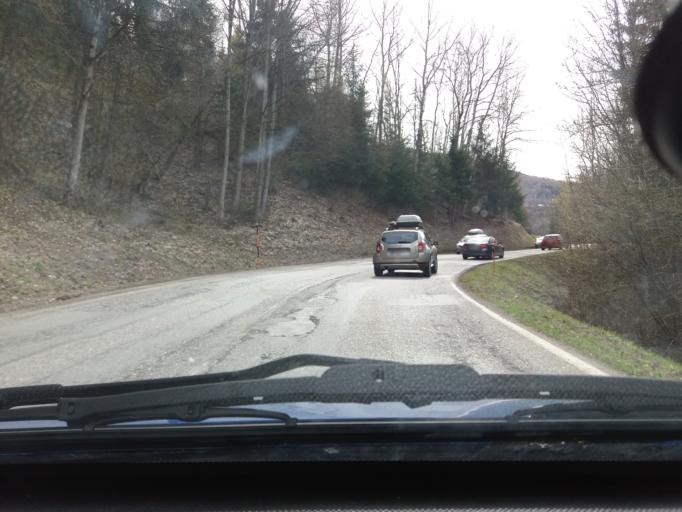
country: FR
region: Rhone-Alpes
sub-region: Departement de la Savoie
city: Macot-la-Plagne
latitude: 45.5470
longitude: 6.6682
